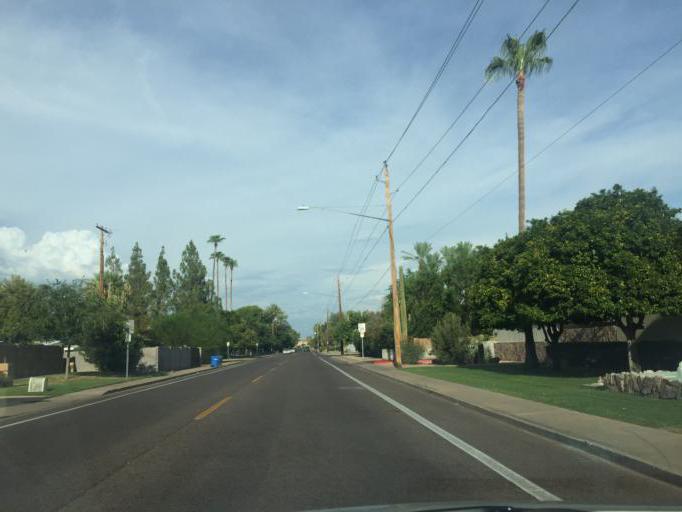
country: US
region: Arizona
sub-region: Maricopa County
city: Phoenix
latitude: 33.5310
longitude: -112.0547
